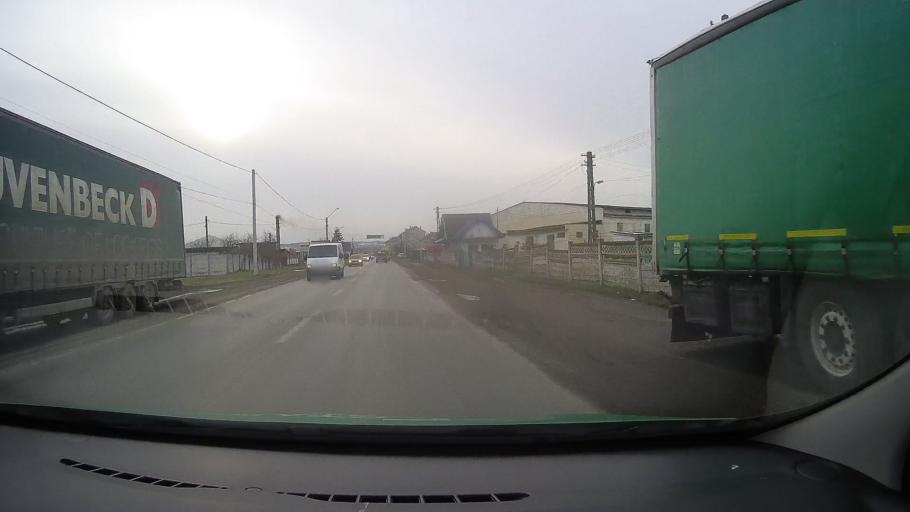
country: RO
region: Hunedoara
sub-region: Municipiul Orastie
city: Orastie
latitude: 45.8596
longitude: 23.2137
